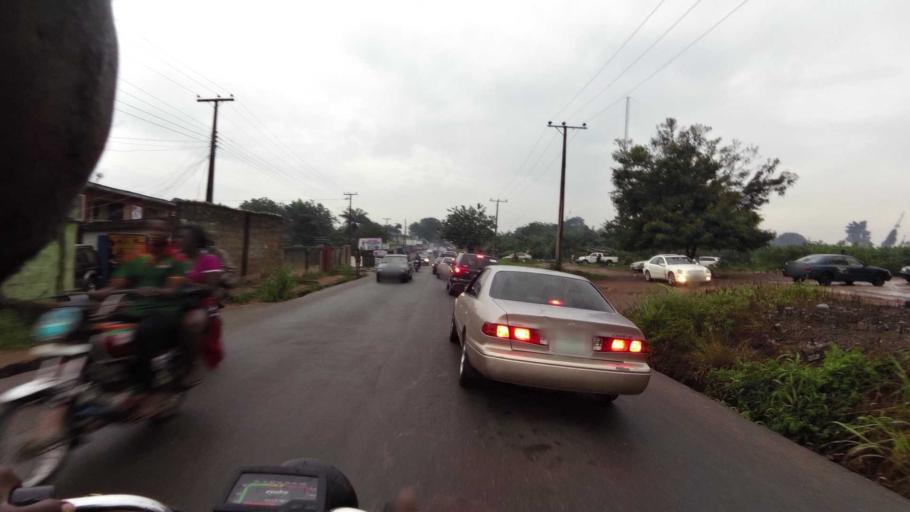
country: NG
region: Oyo
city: Ibadan
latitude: 7.4089
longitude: 3.9289
